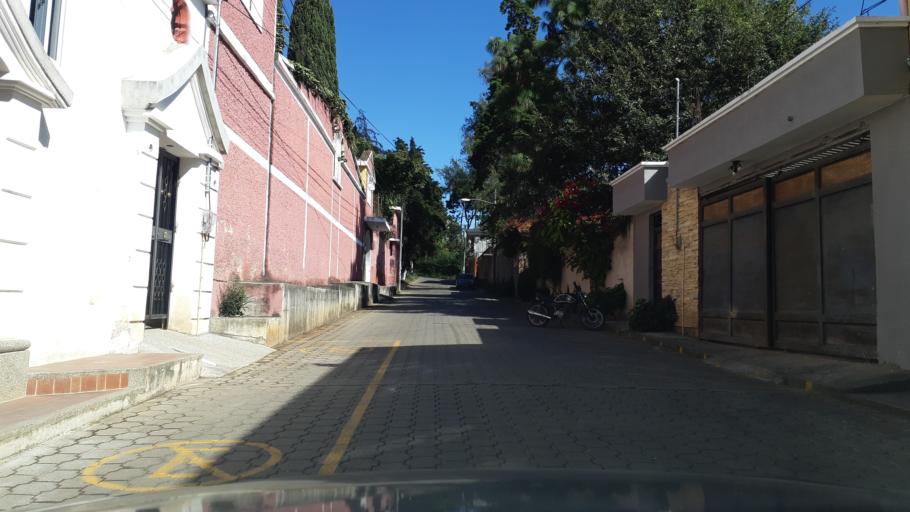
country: GT
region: Chimaltenango
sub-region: Municipio de Chimaltenango
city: Chimaltenango
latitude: 14.6543
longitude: -90.8176
